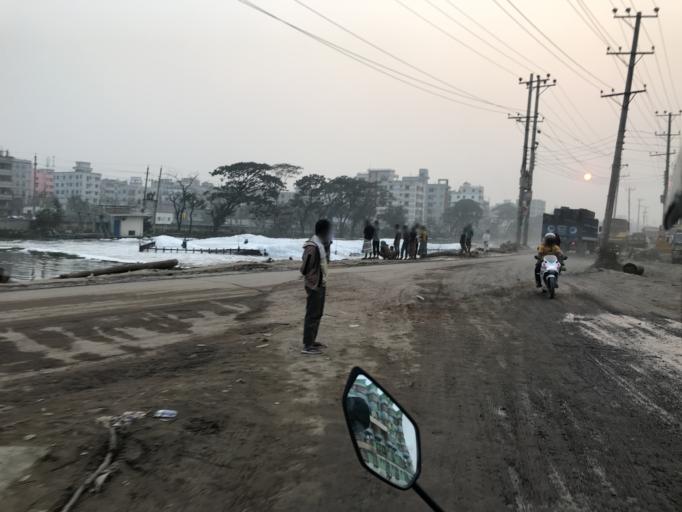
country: BD
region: Dhaka
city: Paltan
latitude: 23.7177
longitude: 90.4742
